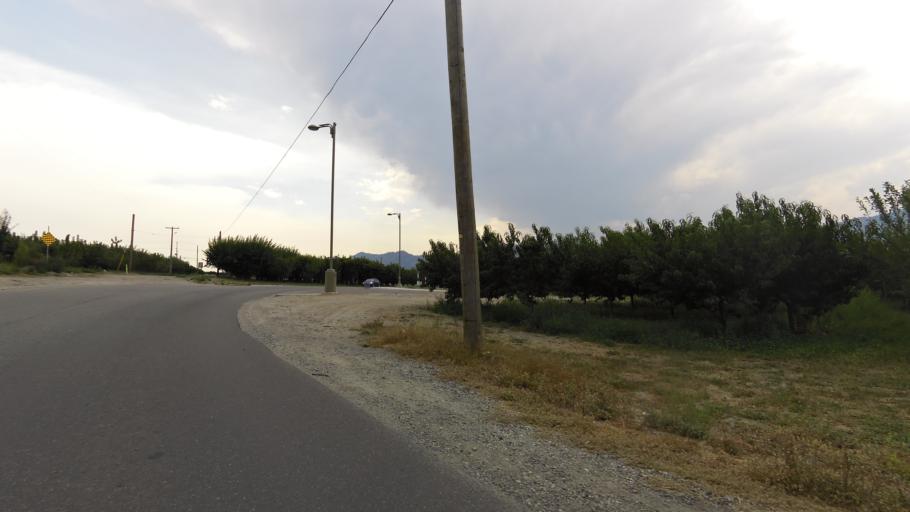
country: CA
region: British Columbia
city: Osoyoos
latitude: 49.0301
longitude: -119.4353
